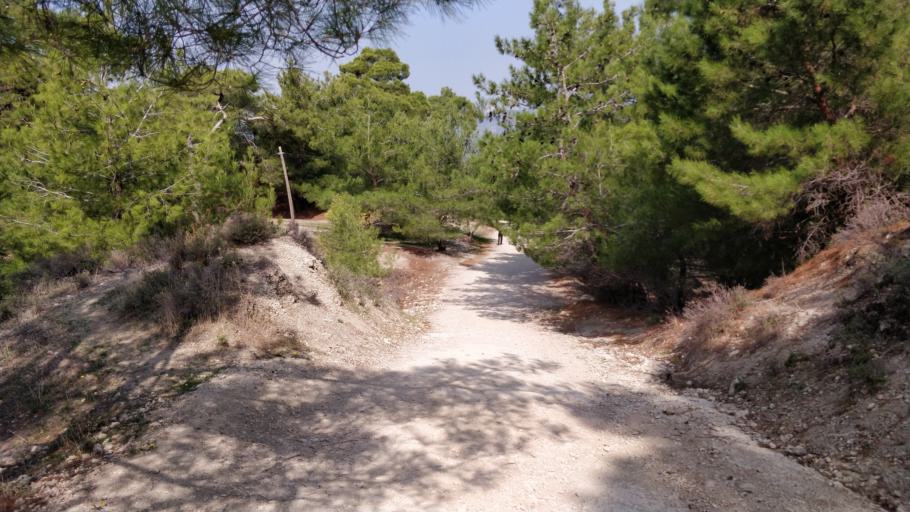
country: TR
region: Canakkale
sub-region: Merkez
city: Kucukkuyu
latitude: 39.5658
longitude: 26.6166
